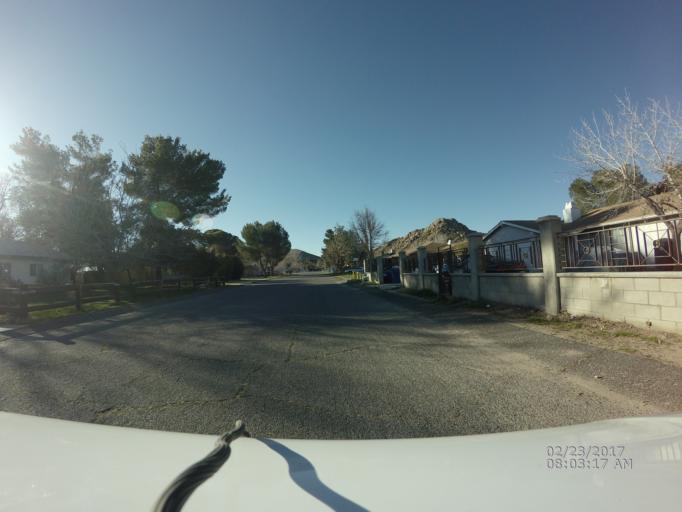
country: US
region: California
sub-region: Los Angeles County
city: Lake Los Angeles
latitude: 34.6136
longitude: -117.8192
